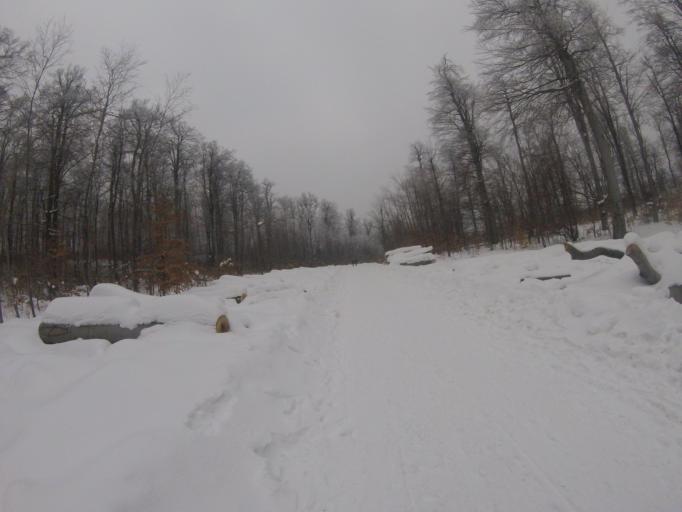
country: HU
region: Pest
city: Pilisszentkereszt
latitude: 47.7122
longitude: 18.8589
